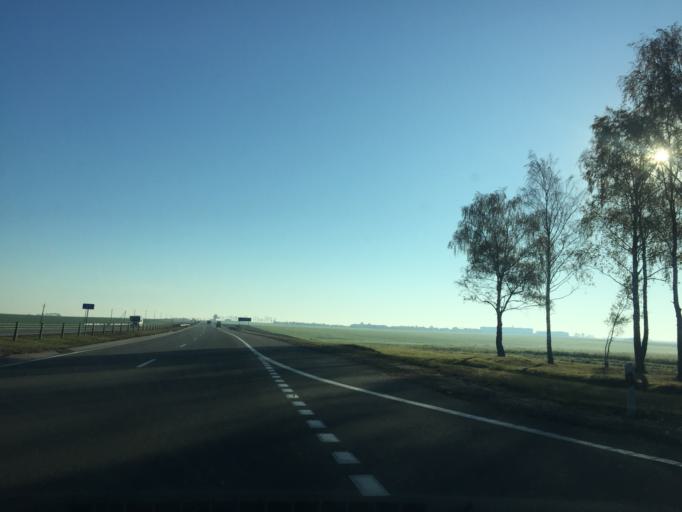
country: BY
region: Minsk
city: Luhavaya Slabada
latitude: 53.7614
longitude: 27.8854
